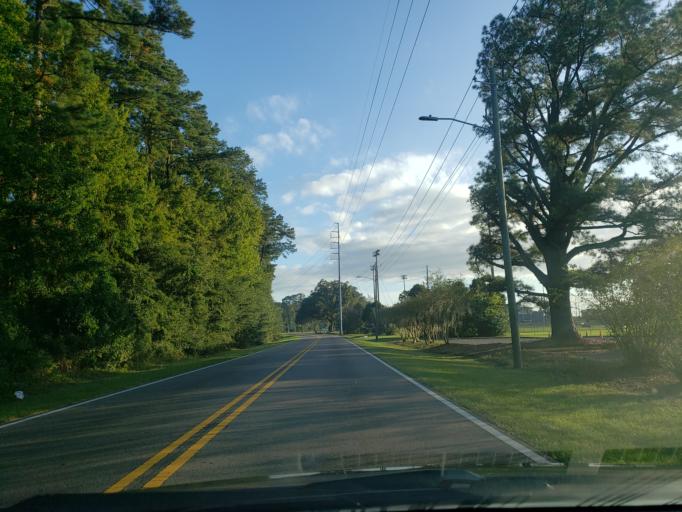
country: US
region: Georgia
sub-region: Chatham County
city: Isle of Hope
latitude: 31.9966
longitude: -81.0782
